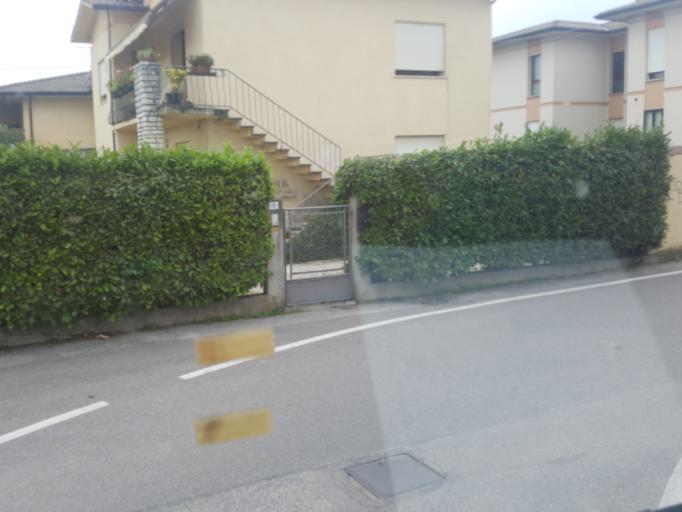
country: IT
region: Veneto
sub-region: Provincia di Vicenza
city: Romano d'Ezzelino
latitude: 45.7695
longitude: 11.7642
